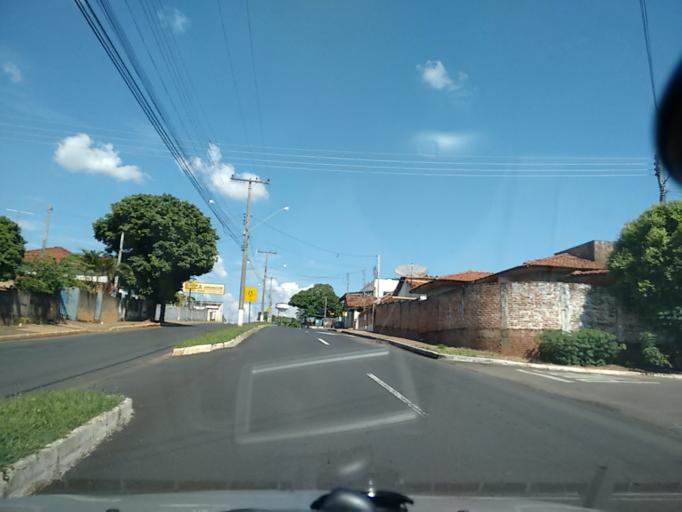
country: BR
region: Sao Paulo
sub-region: Pompeia
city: Pompeia
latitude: -22.0988
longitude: -50.2516
